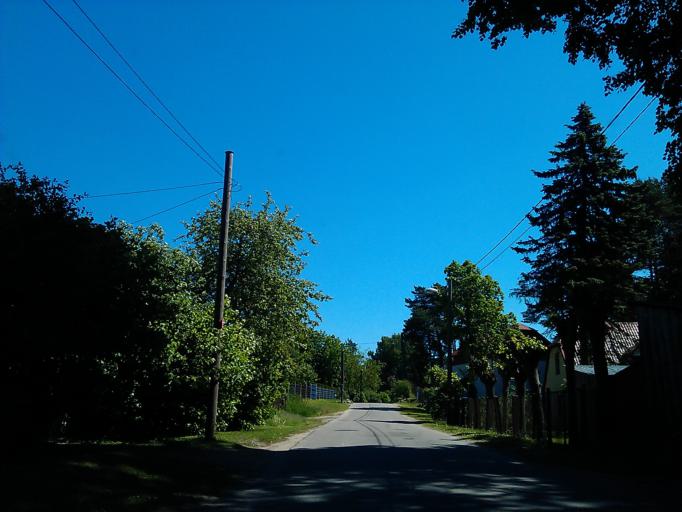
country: LV
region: Riga
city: Bergi
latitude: 56.9966
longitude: 24.2761
